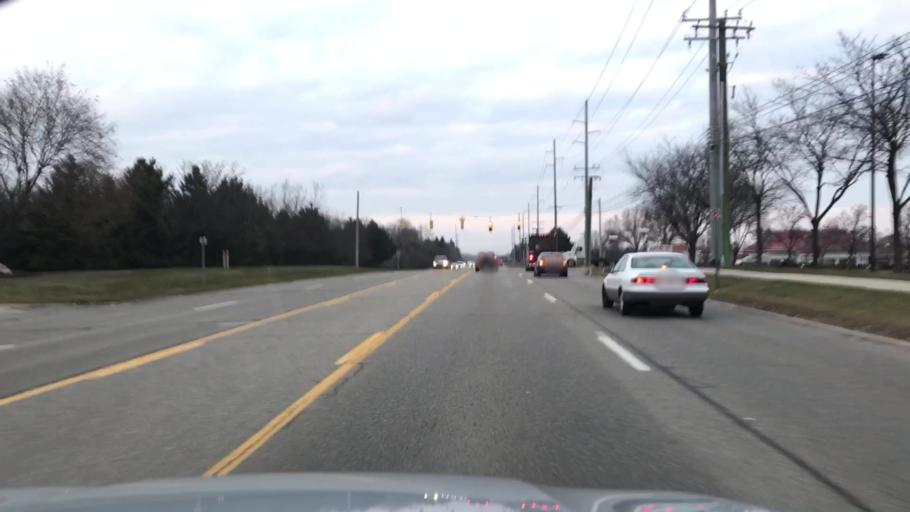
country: US
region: Michigan
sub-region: Wayne County
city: Northville
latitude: 42.4275
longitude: -83.4331
